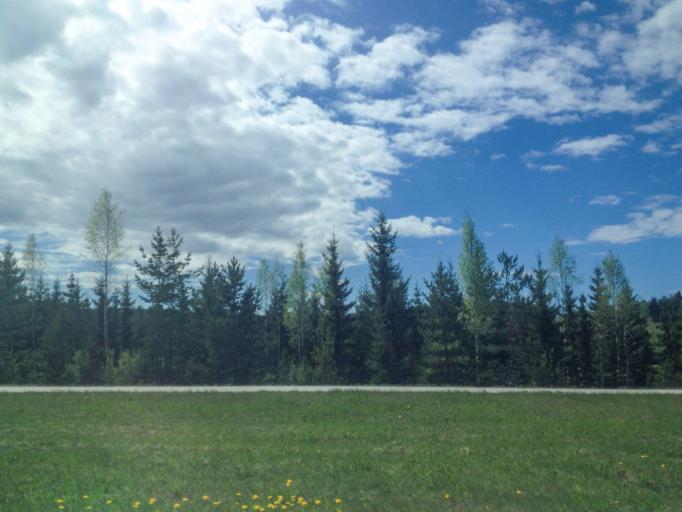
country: FI
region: Haeme
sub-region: Riihimaeki
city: Riihimaeki
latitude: 60.6733
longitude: 24.7737
